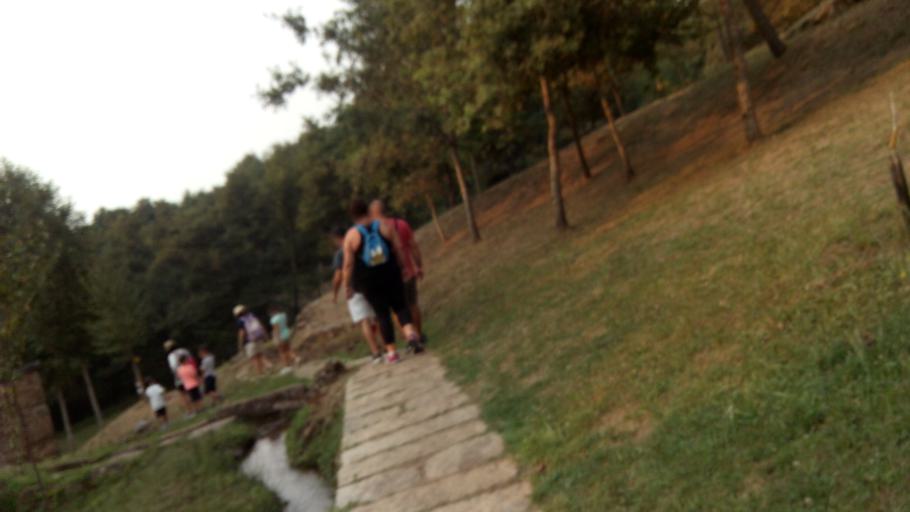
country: ES
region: Galicia
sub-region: Provincia de Pontevedra
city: Porrino
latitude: 42.1580
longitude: -8.6919
